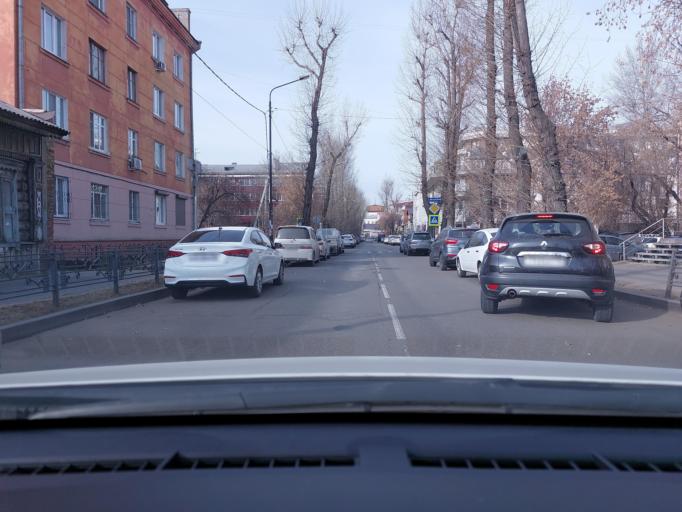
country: RU
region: Irkutsk
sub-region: Irkutskiy Rayon
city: Irkutsk
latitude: 52.2818
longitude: 104.2895
